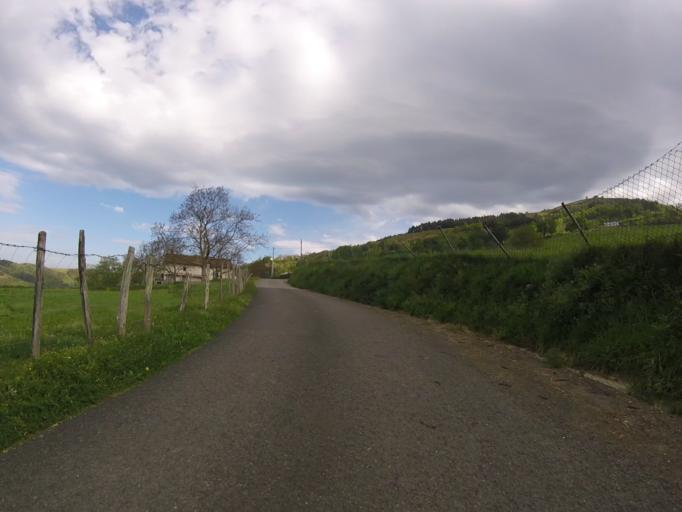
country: ES
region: Basque Country
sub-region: Provincia de Guipuzcoa
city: Aizarnazabal
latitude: 43.2532
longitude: -2.2292
